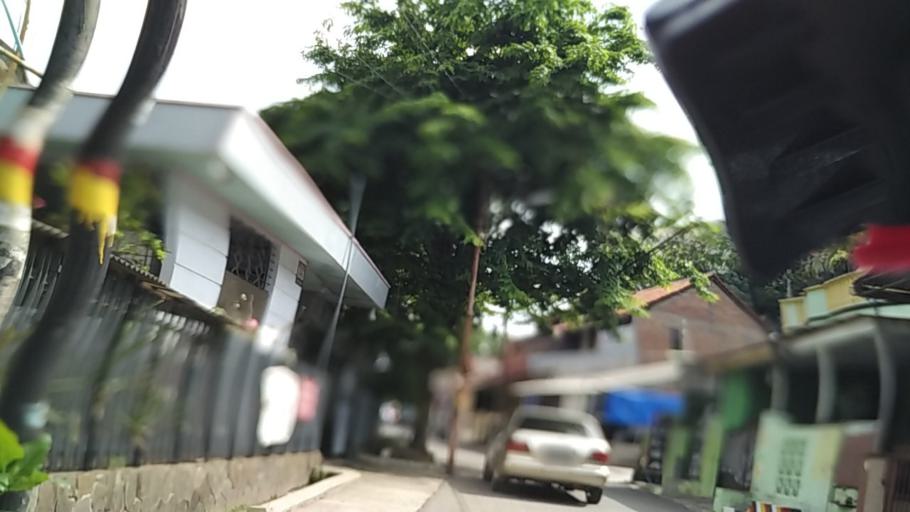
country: ID
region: Central Java
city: Semarang
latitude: -6.9985
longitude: 110.4241
